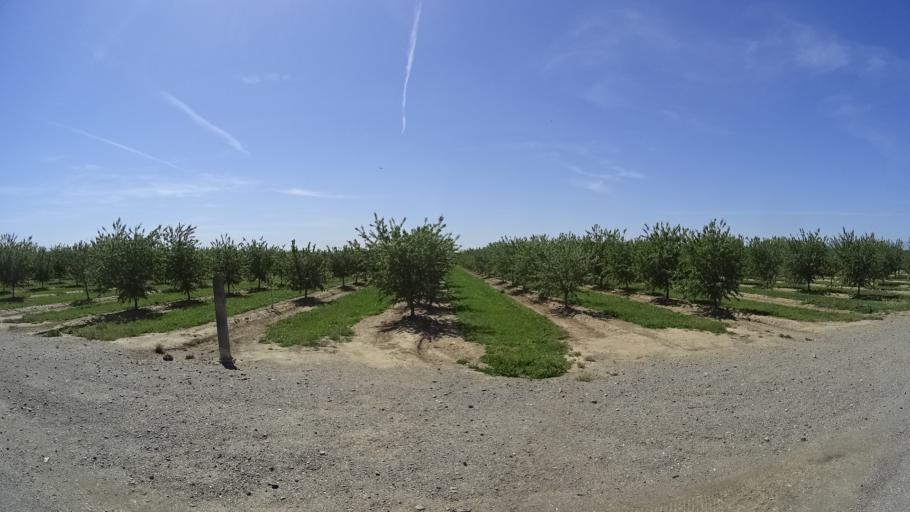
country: US
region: California
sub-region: Glenn County
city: Orland
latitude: 39.6382
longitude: -122.1296
